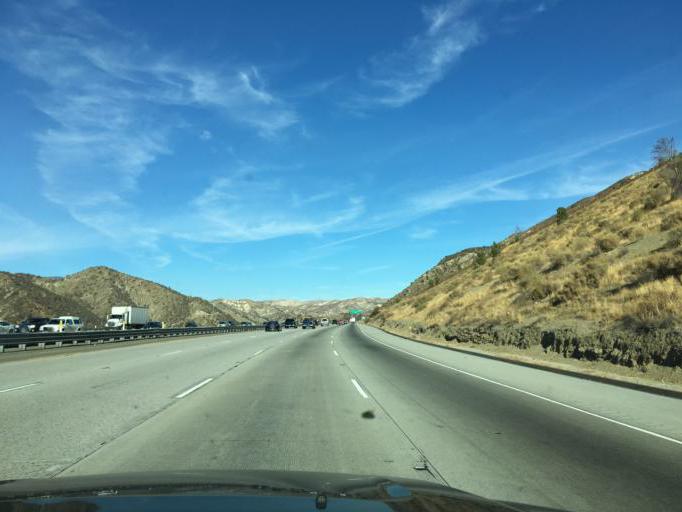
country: US
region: California
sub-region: Kern County
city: Lebec
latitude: 34.6887
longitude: -118.7869
